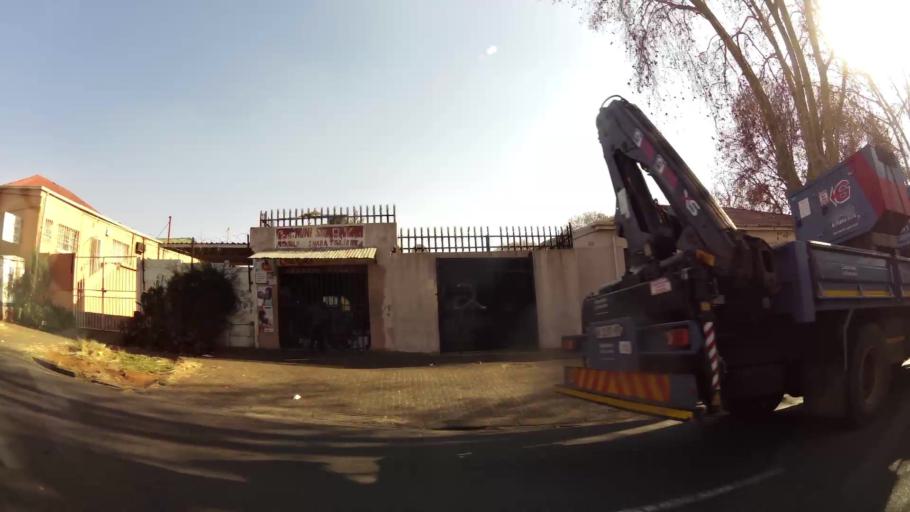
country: ZA
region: Gauteng
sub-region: City of Johannesburg Metropolitan Municipality
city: Johannesburg
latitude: -26.1896
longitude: 28.0864
